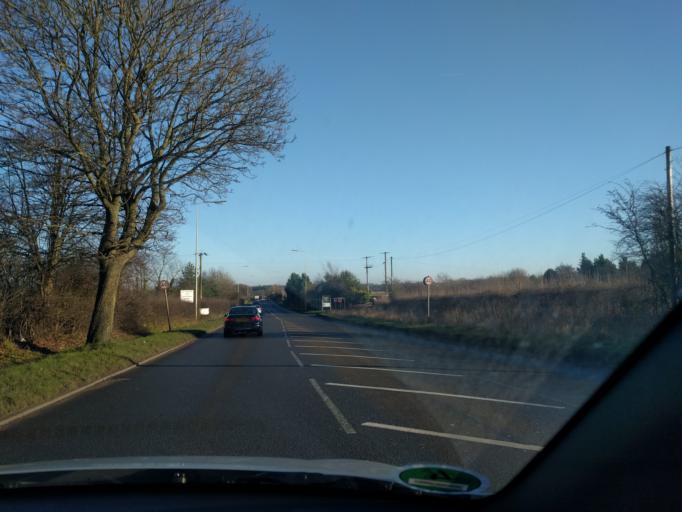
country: GB
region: England
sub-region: Staffordshire
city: Featherstone
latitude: 52.6544
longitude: -2.0759
